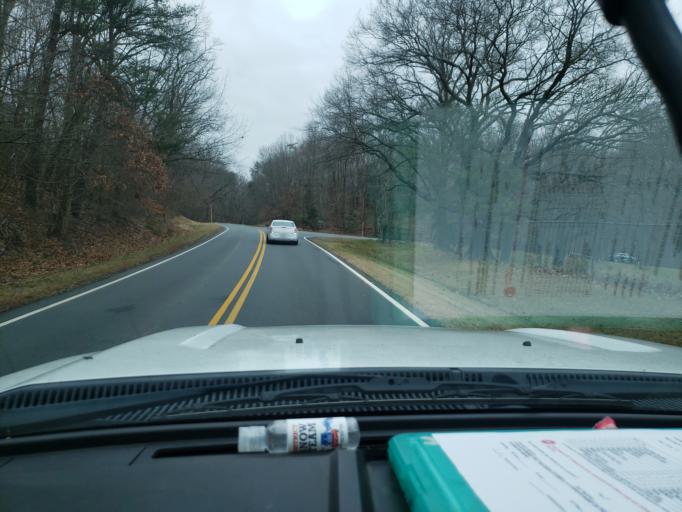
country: US
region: Maryland
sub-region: Prince George's County
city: Coral Hills
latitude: 38.8771
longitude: -76.9495
